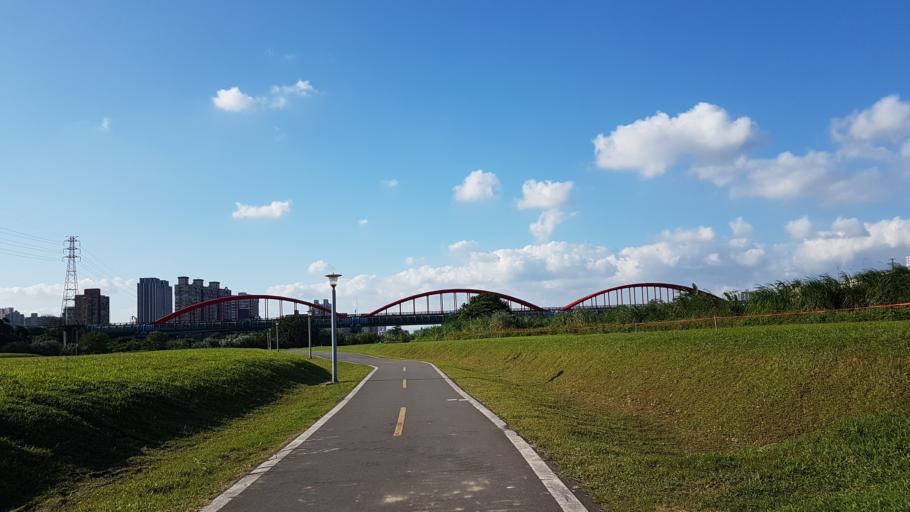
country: TW
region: Taipei
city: Taipei
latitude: 25.0084
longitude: 121.5290
